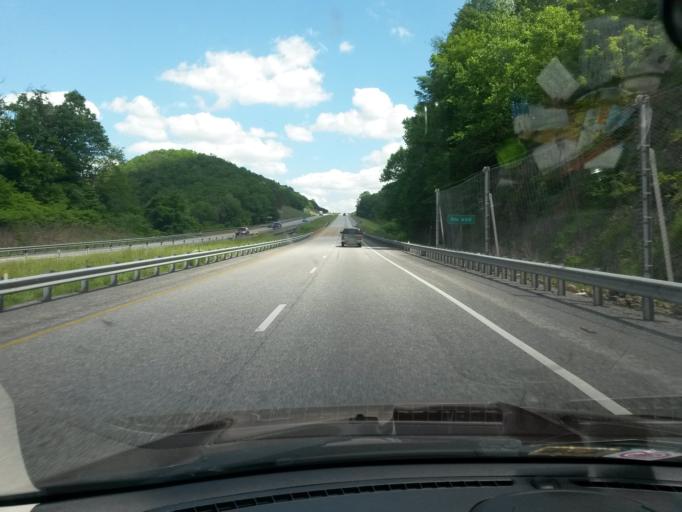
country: US
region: Virginia
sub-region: City of Covington
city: Covington
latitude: 37.7972
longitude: -80.0519
